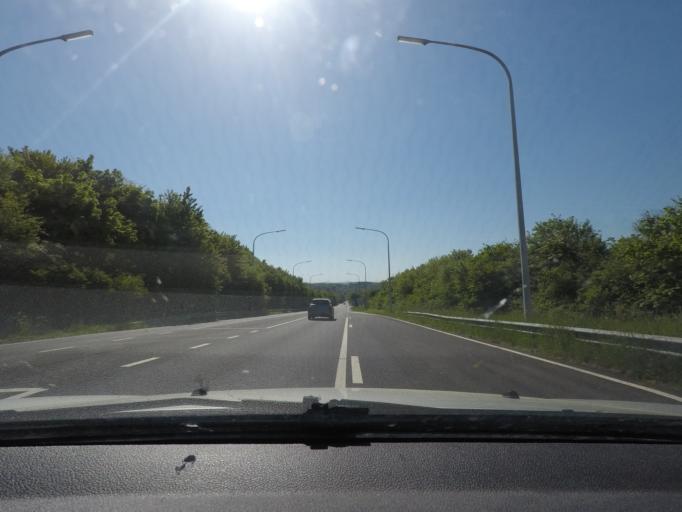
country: BE
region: Wallonia
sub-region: Province de Namur
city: Houyet
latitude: 50.1688
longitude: 5.0718
